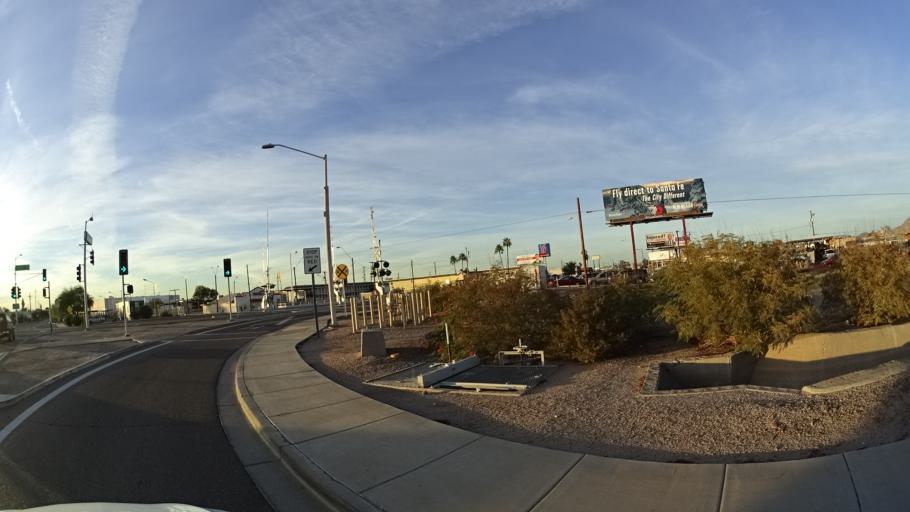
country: US
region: Arizona
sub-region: Maricopa County
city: Phoenix
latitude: 33.4440
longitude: -112.0298
